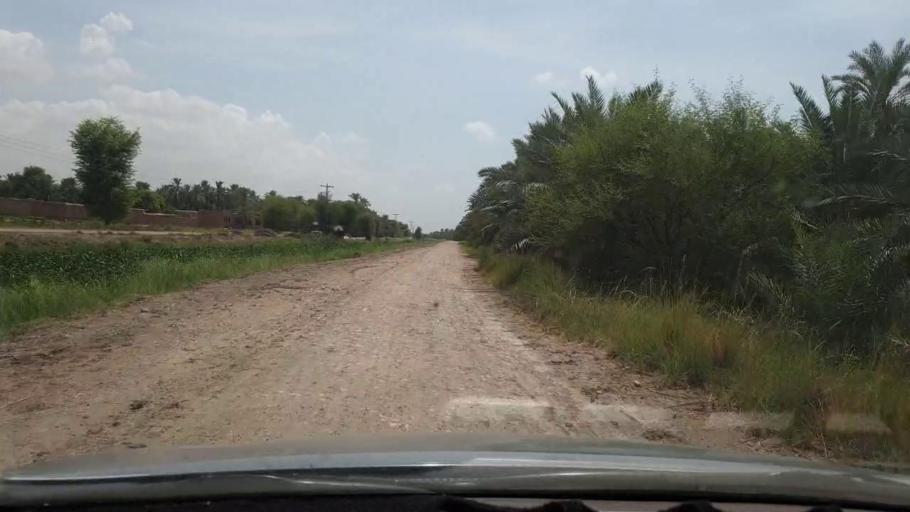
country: PK
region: Sindh
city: Khairpur
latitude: 27.4652
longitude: 68.7954
